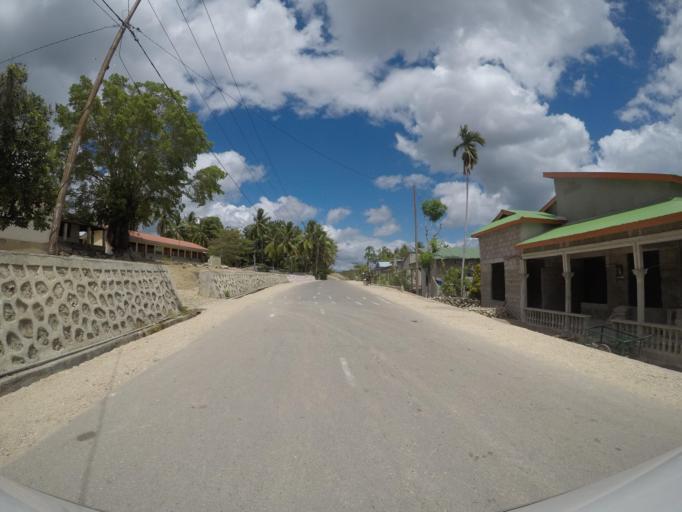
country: TL
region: Lautem
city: Lospalos
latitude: -8.3608
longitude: 126.9307
